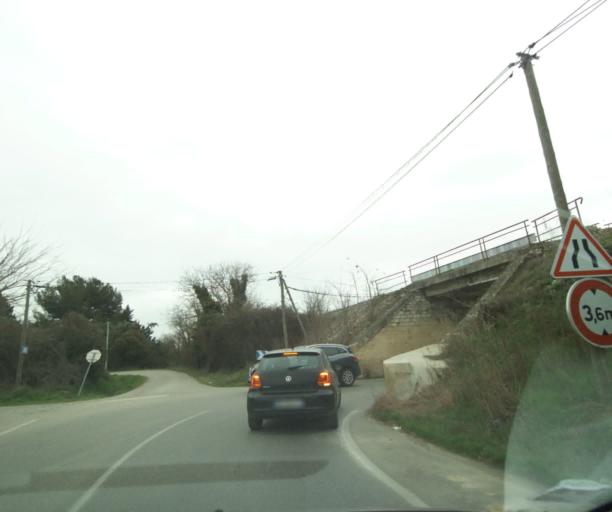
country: FR
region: Provence-Alpes-Cote d'Azur
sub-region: Departement des Bouches-du-Rhone
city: Venelles
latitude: 43.5794
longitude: 5.4489
